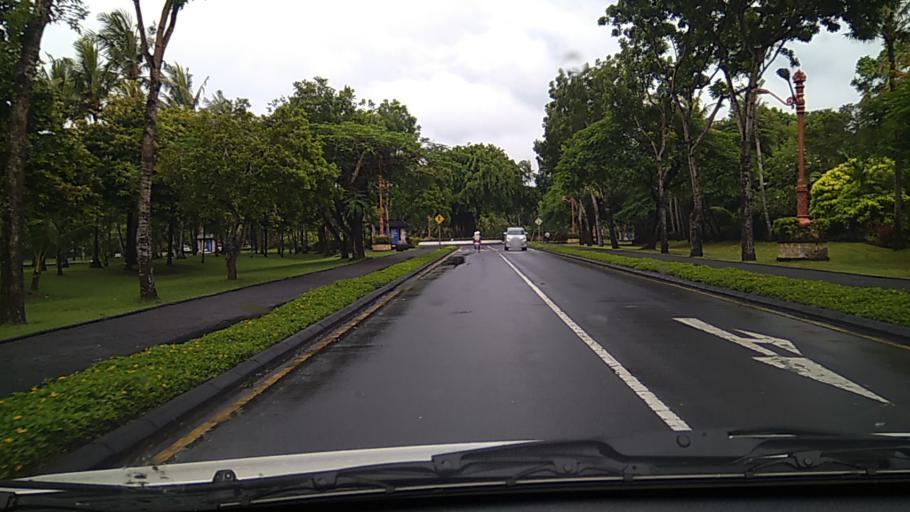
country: ID
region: Bali
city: Bualu
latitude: -8.8028
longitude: 115.2288
